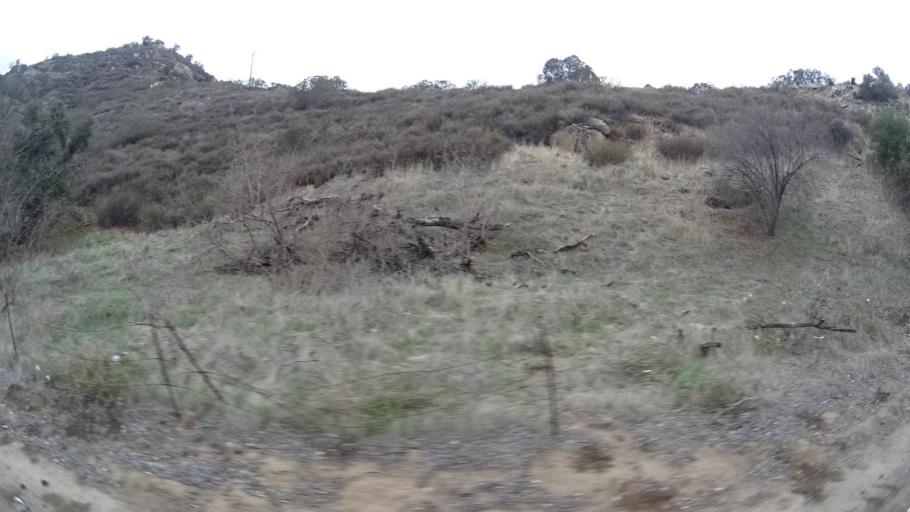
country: US
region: California
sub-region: San Diego County
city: Harbison Canyon
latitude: 32.8915
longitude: -116.8430
